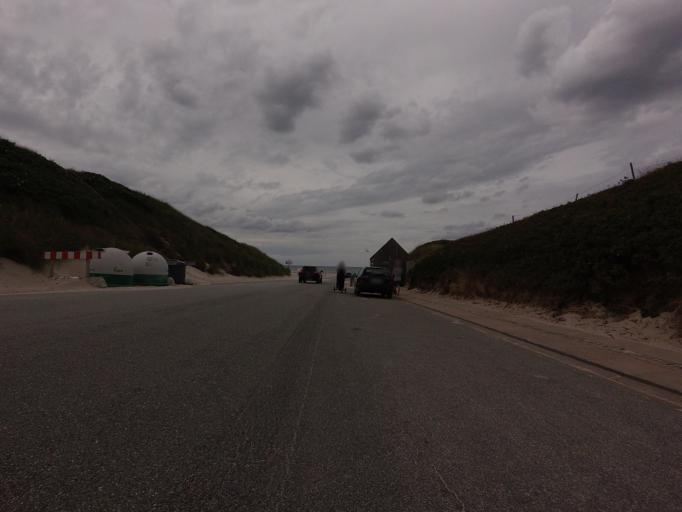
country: DK
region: North Denmark
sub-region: Jammerbugt Kommune
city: Pandrup
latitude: 57.3623
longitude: 9.7004
